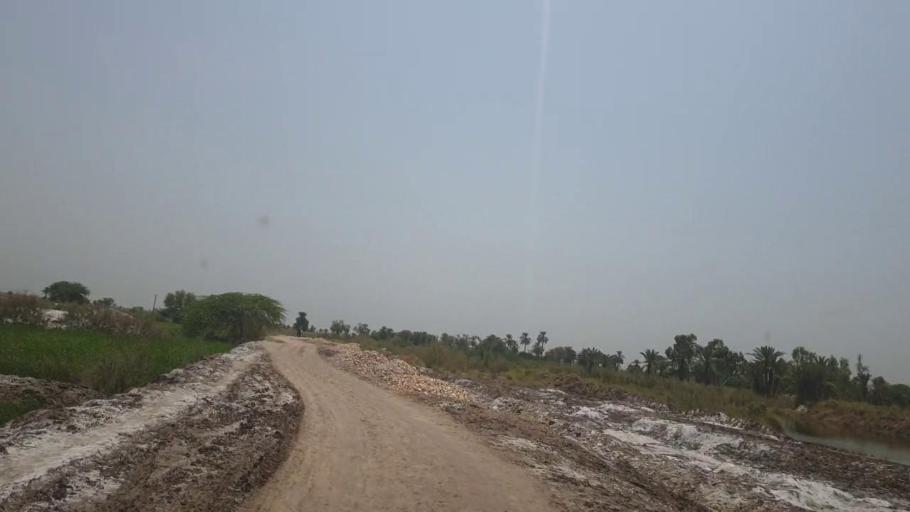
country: PK
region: Sindh
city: Lakhi
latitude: 27.8623
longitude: 68.6634
